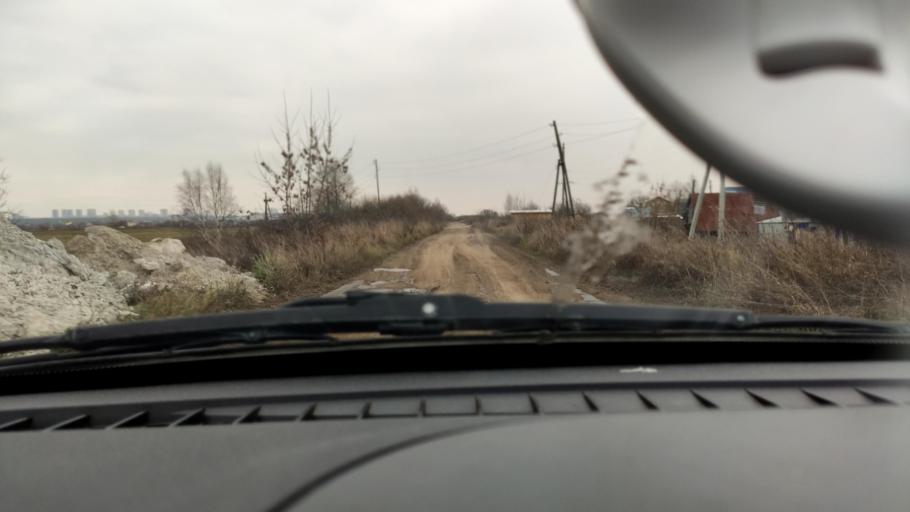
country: RU
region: Perm
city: Kondratovo
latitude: 57.9893
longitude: 56.0770
